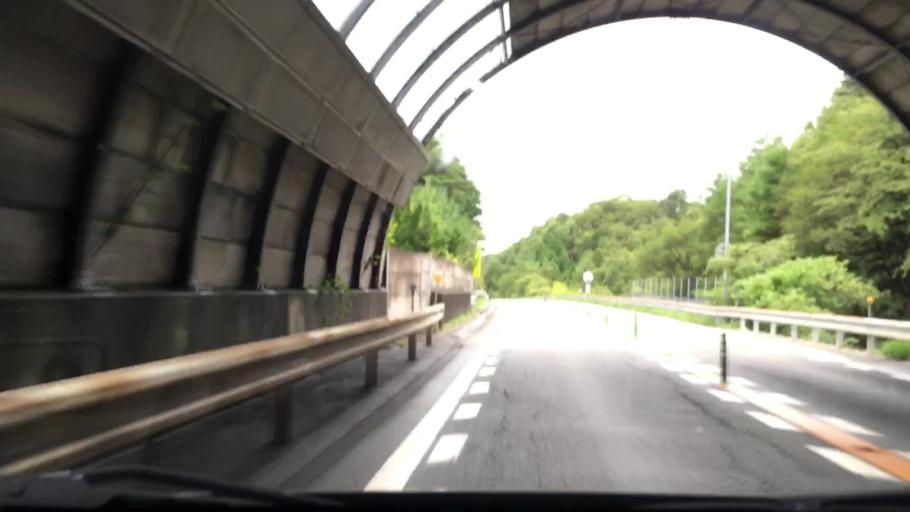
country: JP
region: Hyogo
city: Nishiwaki
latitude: 35.0780
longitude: 134.7715
